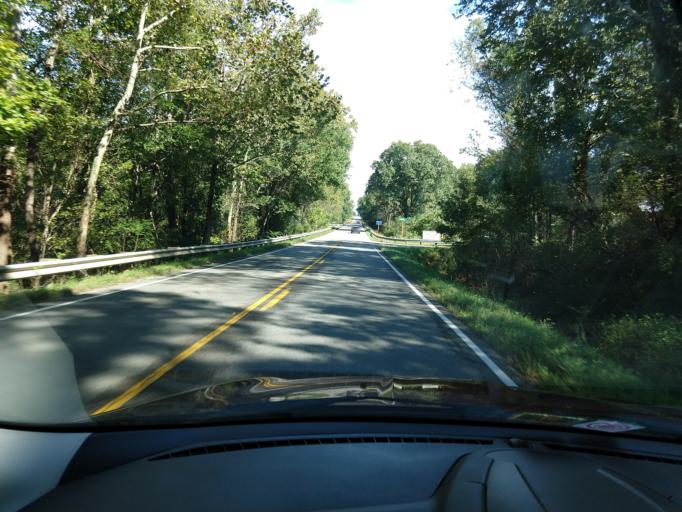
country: US
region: Virginia
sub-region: Augusta County
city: Crimora
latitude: 38.1839
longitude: -78.8423
